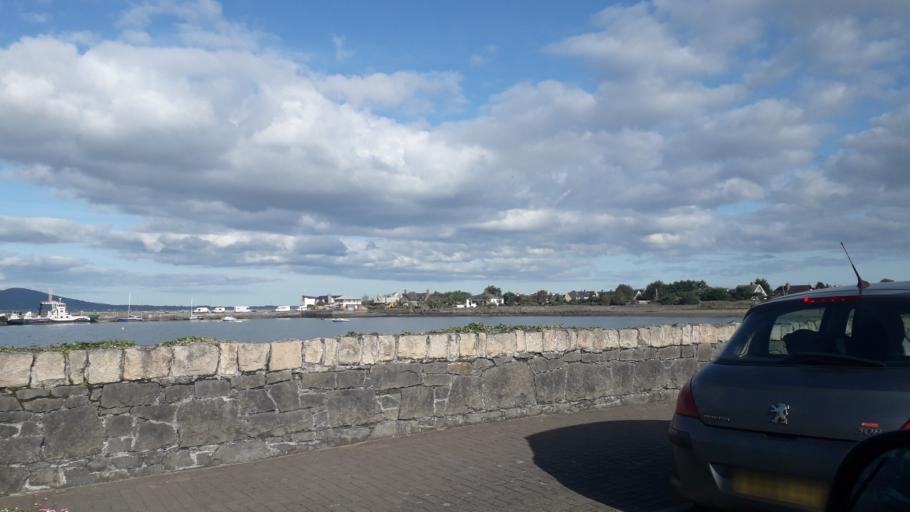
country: IE
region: Leinster
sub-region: Lu
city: Carlingford
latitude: 54.0413
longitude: -6.1859
